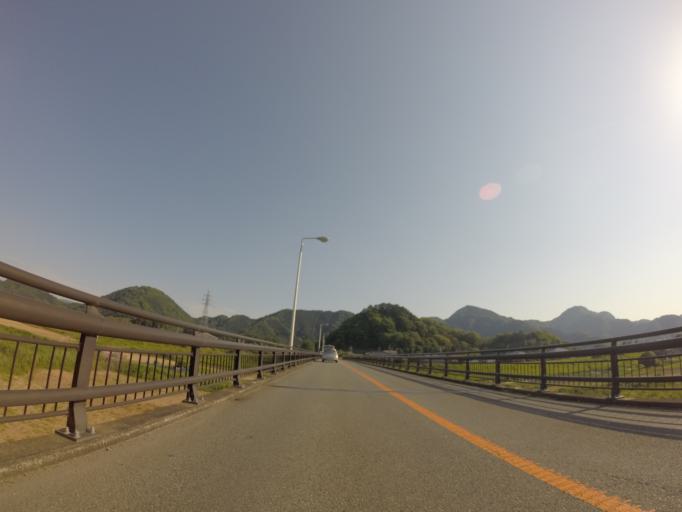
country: JP
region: Shizuoka
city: Mishima
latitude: 35.0753
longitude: 138.9191
